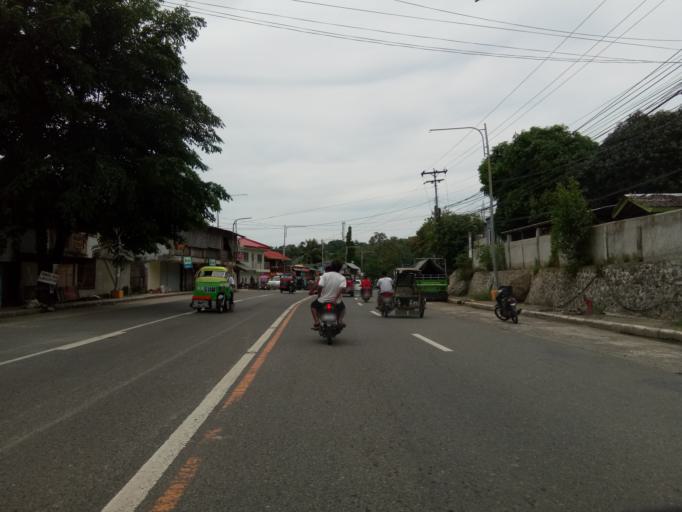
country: PH
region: Caraga
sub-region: Province of Surigao del Norte
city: Surigao
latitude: 9.7791
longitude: 125.4833
